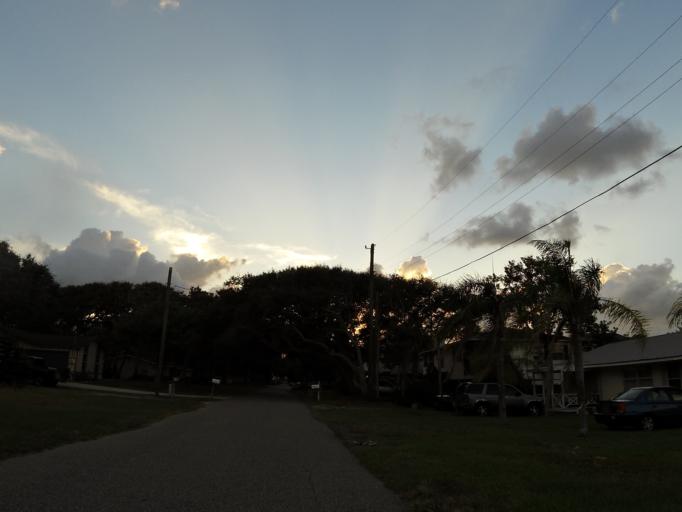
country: US
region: Florida
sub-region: Saint Johns County
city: Villano Beach
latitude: 29.9238
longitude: -81.2977
